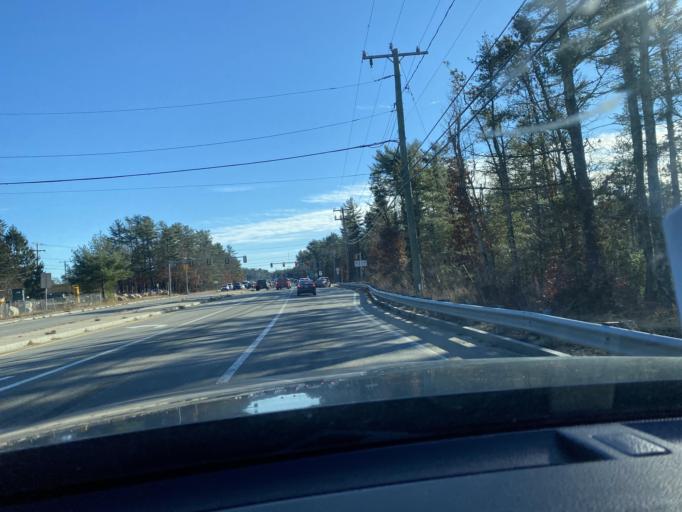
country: US
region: Massachusetts
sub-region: Plymouth County
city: West Wareham
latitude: 41.7798
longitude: -70.7432
